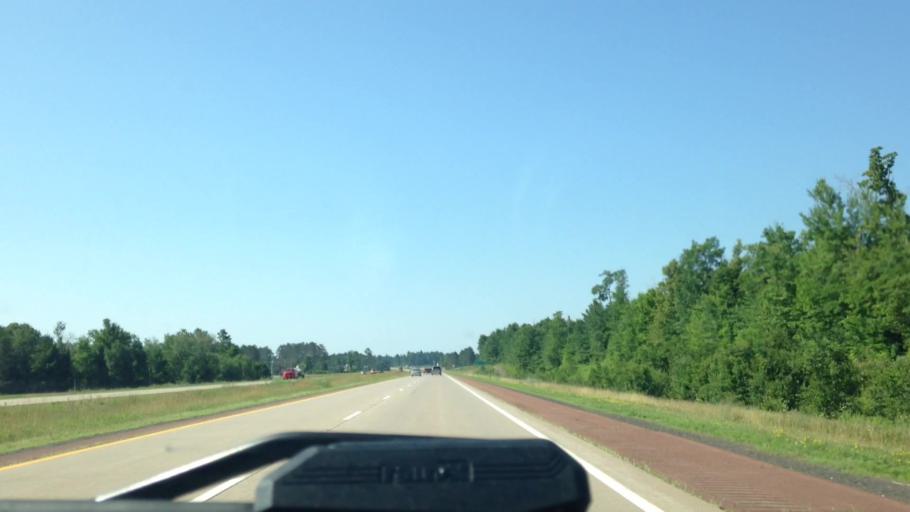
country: US
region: Wisconsin
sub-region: Douglas County
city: Lake Nebagamon
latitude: 46.3652
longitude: -91.8302
